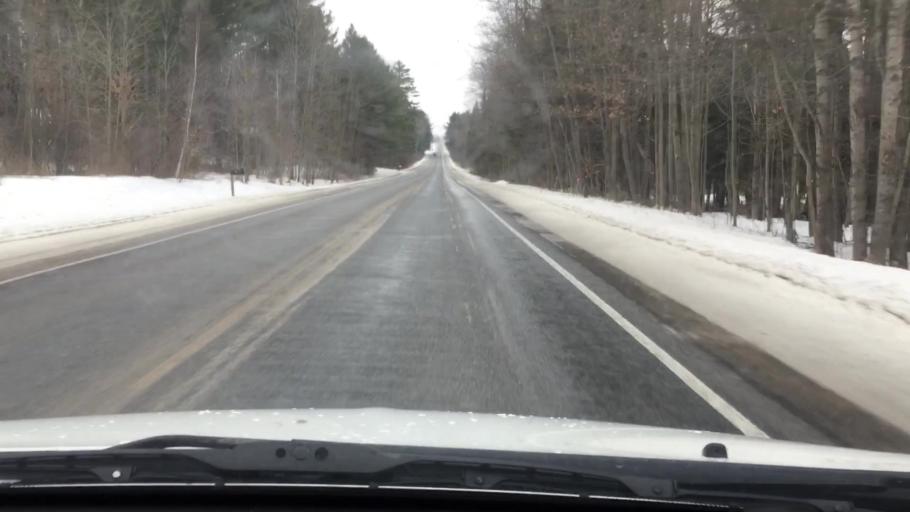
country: US
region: Michigan
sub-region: Osceola County
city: Reed City
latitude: 44.0585
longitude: -85.4440
